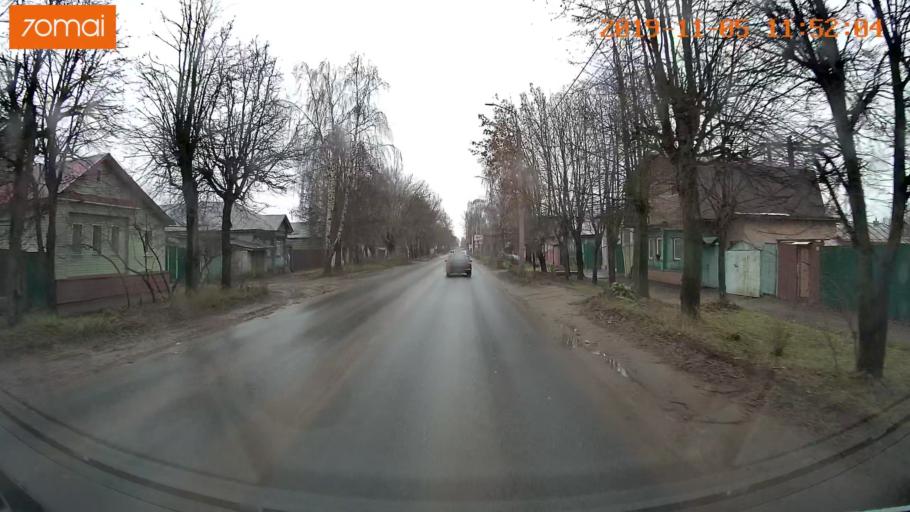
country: RU
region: Ivanovo
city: Bogorodskoye
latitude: 57.0019
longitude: 41.0291
